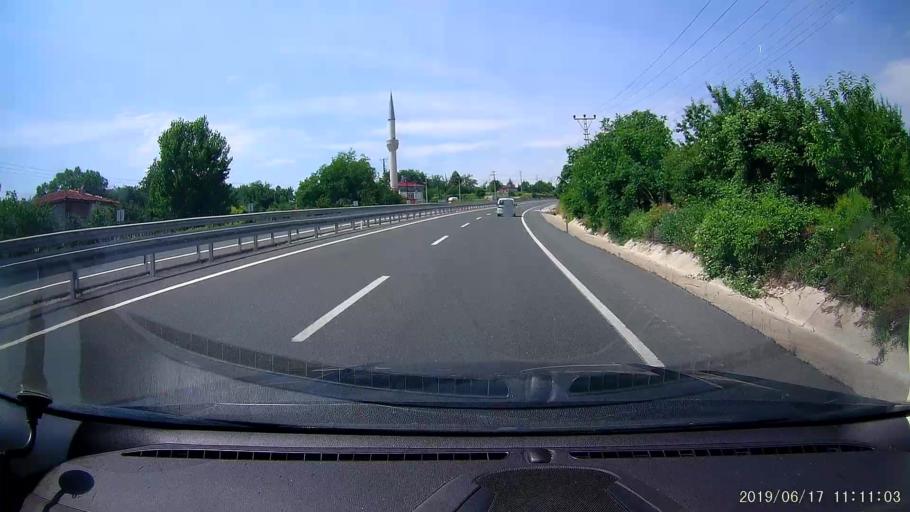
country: TR
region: Kastamonu
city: Tosya
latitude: 40.9916
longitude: 34.0147
